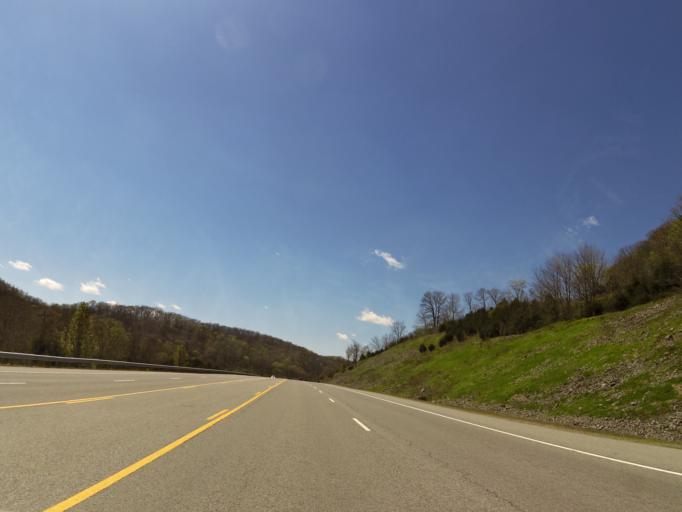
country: US
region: Tennessee
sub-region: DeKalb County
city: Smithville
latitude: 36.0015
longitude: -85.9100
